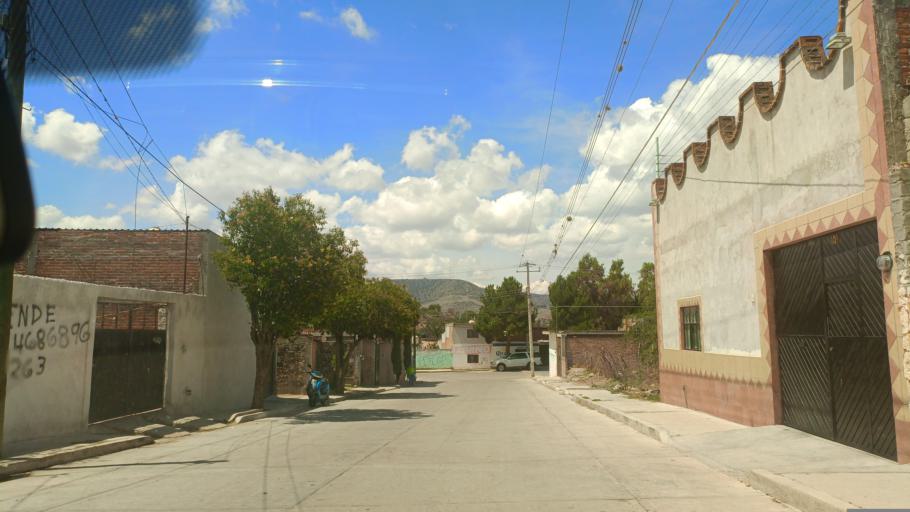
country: MX
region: Guanajuato
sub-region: San Luis de la Paz
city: San Luis de la Paz
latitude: 21.3028
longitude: -100.5073
